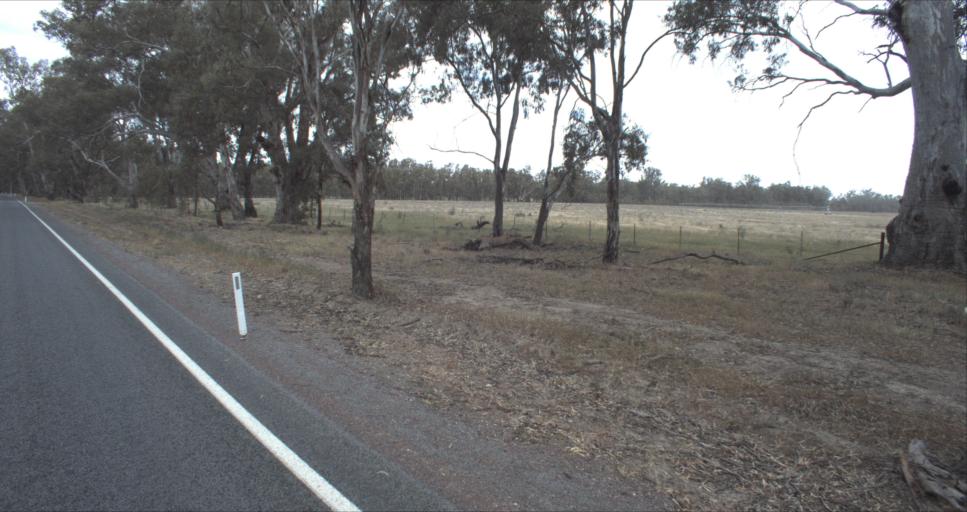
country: AU
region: New South Wales
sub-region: Leeton
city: Leeton
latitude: -34.6411
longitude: 146.3640
